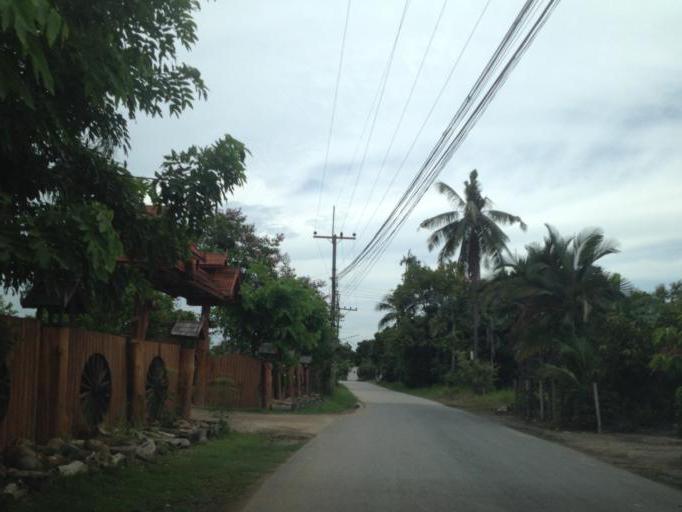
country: TH
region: Chiang Mai
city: Hang Dong
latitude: 18.6922
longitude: 98.8714
